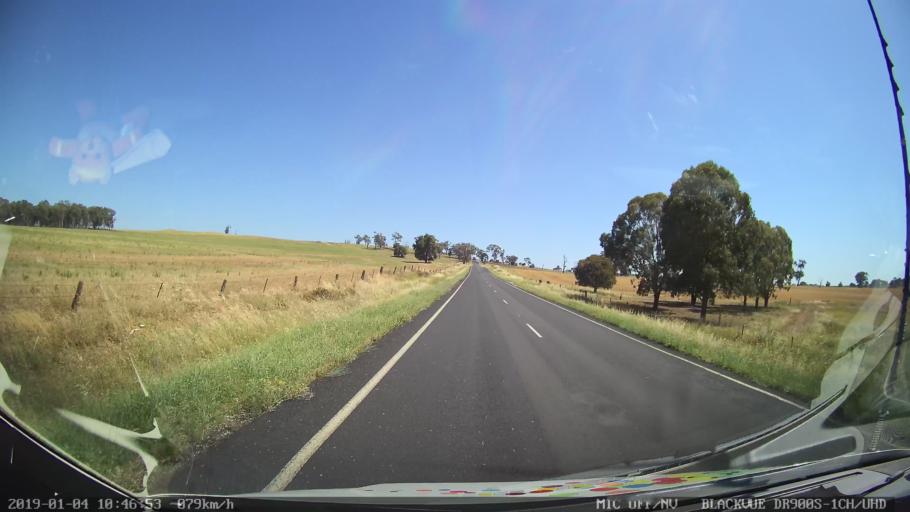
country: AU
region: New South Wales
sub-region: Cabonne
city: Molong
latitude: -33.2760
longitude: 148.7210
